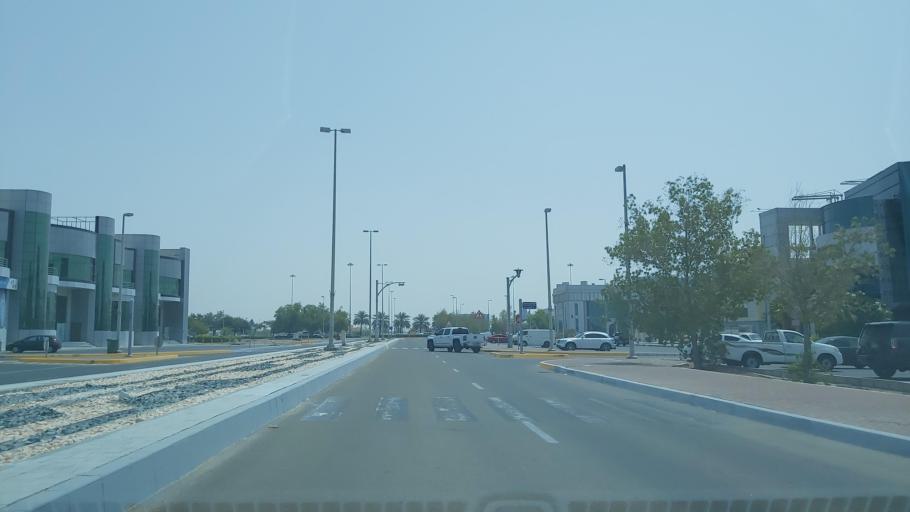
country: AE
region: Abu Dhabi
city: Abu Dhabi
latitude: 24.3783
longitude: 54.5216
